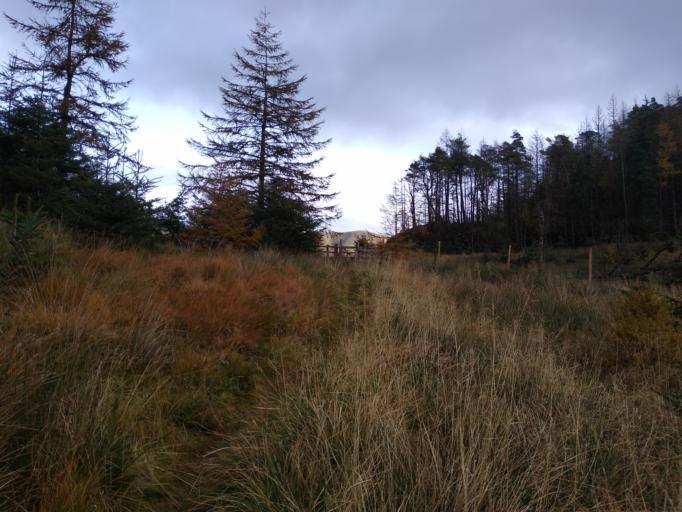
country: GB
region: England
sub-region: Cumbria
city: Keswick
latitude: 54.5607
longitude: -3.0820
